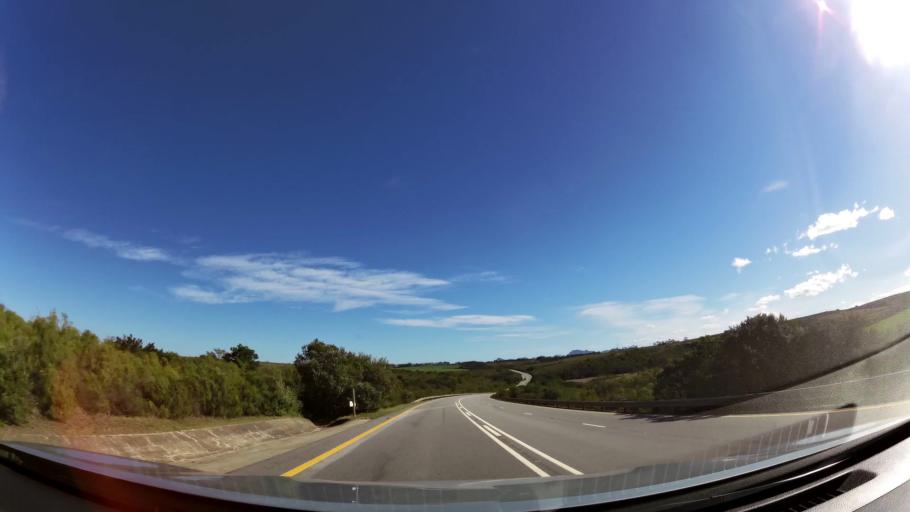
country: ZA
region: Eastern Cape
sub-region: Cacadu District Municipality
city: Kruisfontein
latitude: -34.0132
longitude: 24.6421
